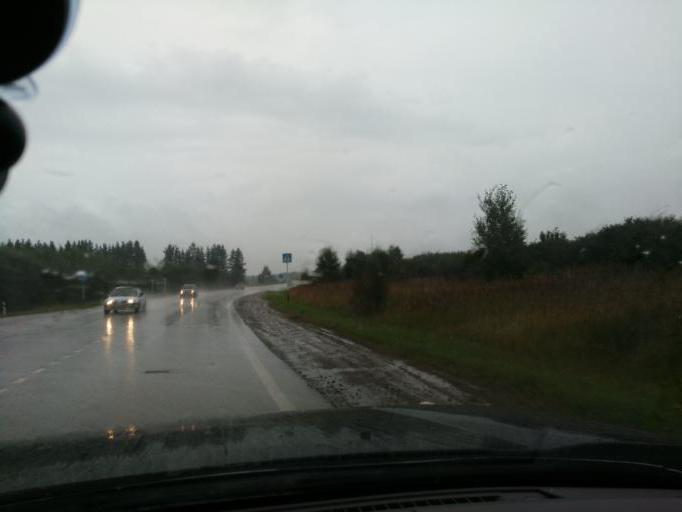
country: RU
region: Perm
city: Osa
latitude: 57.3319
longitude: 55.5850
